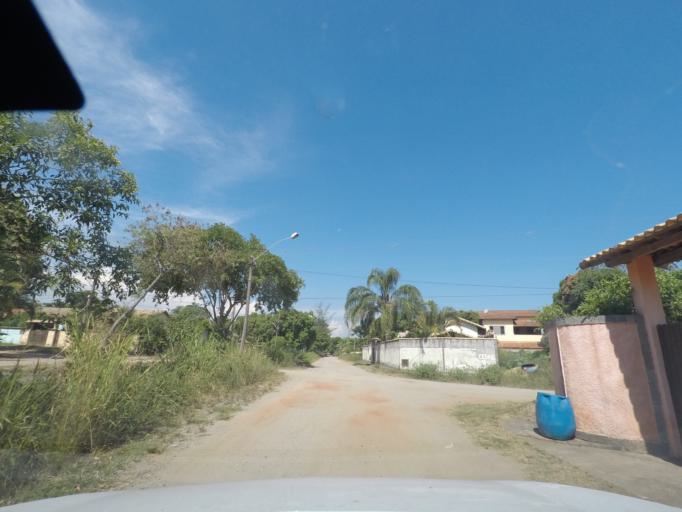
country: BR
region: Rio de Janeiro
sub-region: Niteroi
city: Niteroi
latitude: -22.9557
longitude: -42.9680
